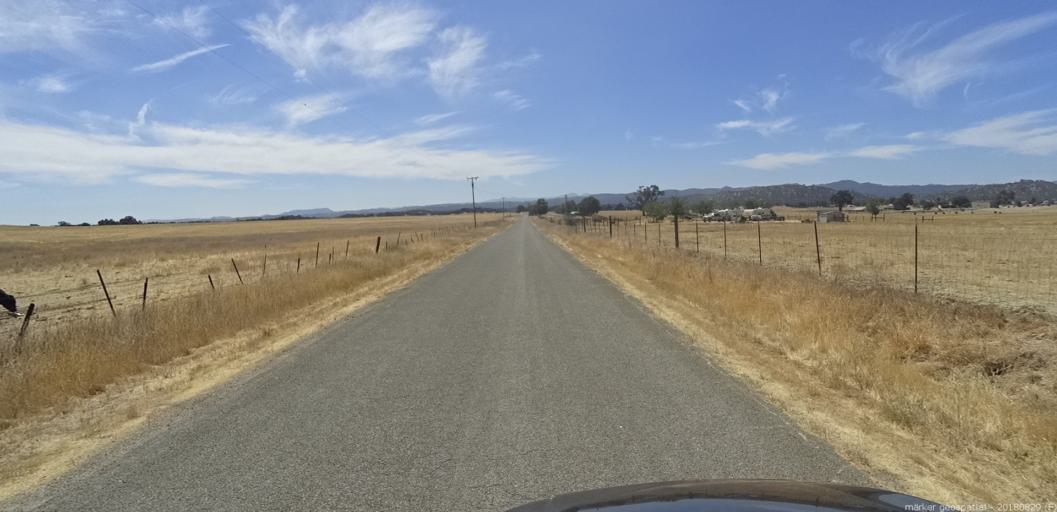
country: US
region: California
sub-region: San Luis Obispo County
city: Lake Nacimiento
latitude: 35.9360
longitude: -121.0643
